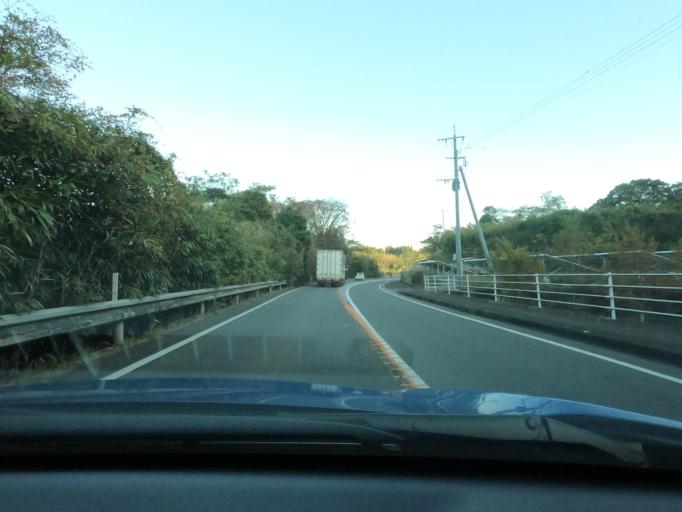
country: JP
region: Kagoshima
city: Satsumasendai
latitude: 31.8437
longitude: 130.2785
